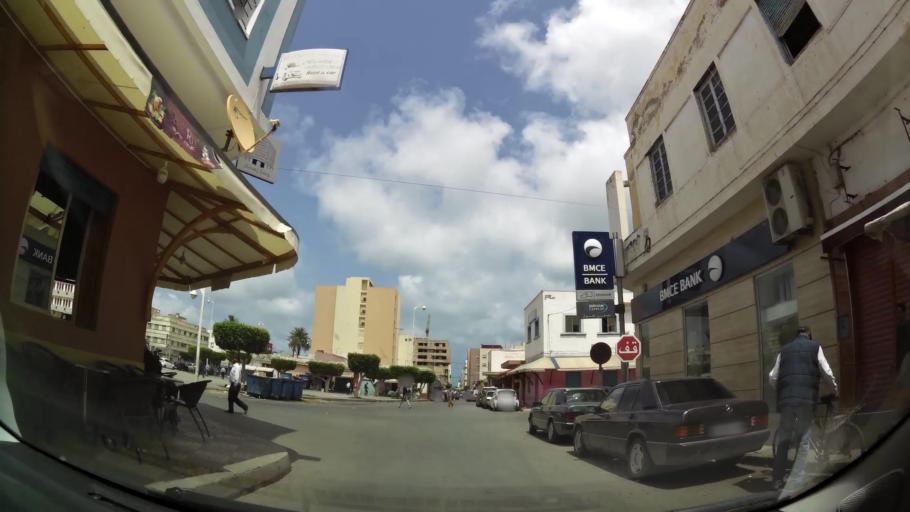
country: MA
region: Oriental
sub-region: Nador
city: Nador
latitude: 35.1785
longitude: -2.9274
